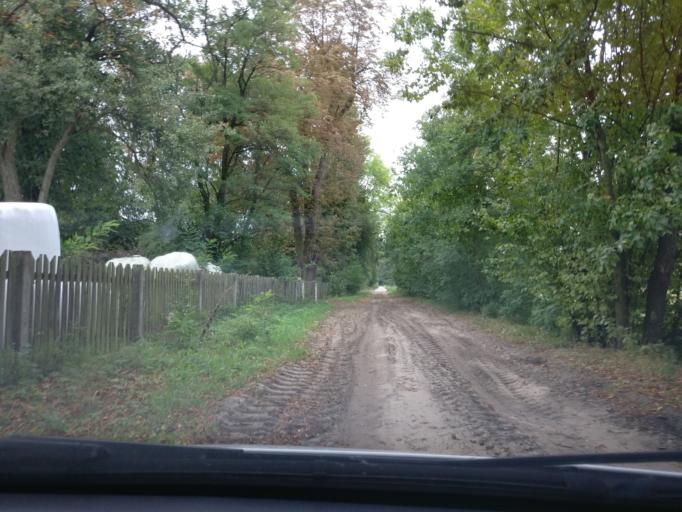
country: PL
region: Masovian Voivodeship
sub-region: Powiat kozienicki
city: Garbatka-Letnisko
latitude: 51.5129
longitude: 21.5984
